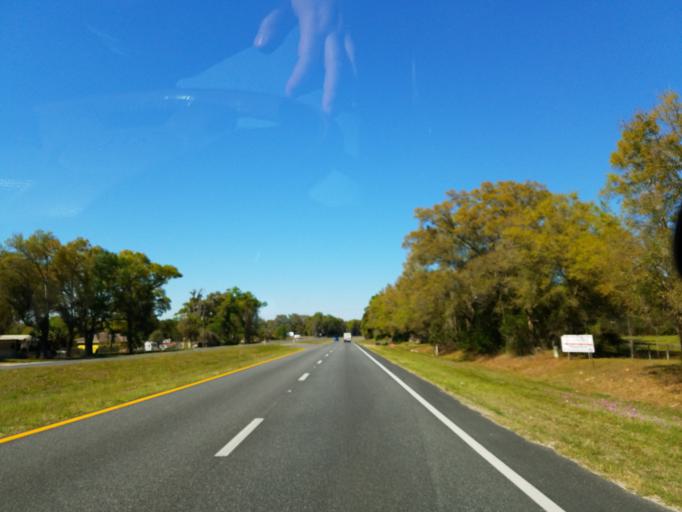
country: US
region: Florida
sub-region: Marion County
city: Belleview
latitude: 29.0177
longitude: -82.0446
